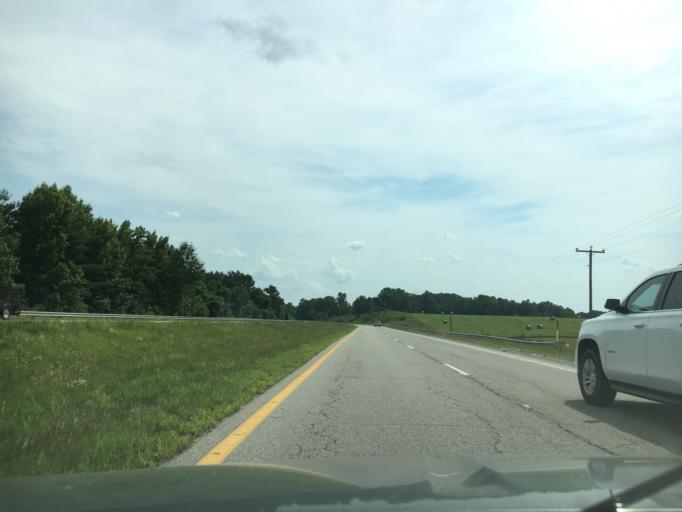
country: US
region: Virginia
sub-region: Nottoway County
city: Crewe
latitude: 37.1796
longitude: -78.2417
